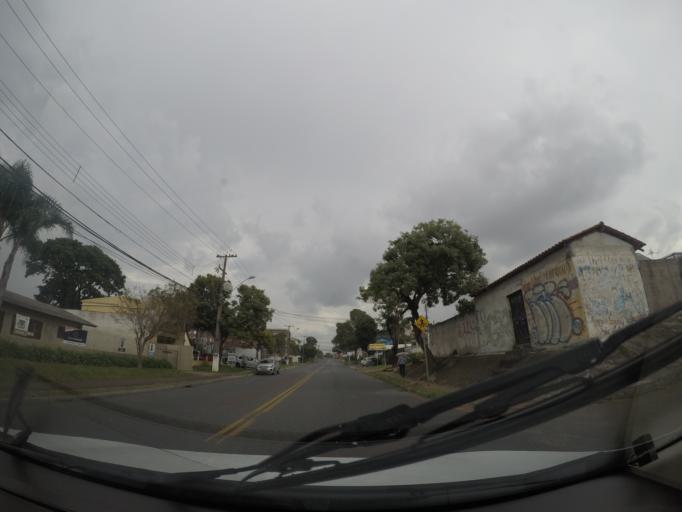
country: BR
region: Parana
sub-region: Sao Jose Dos Pinhais
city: Sao Jose dos Pinhais
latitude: -25.5249
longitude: -49.2363
